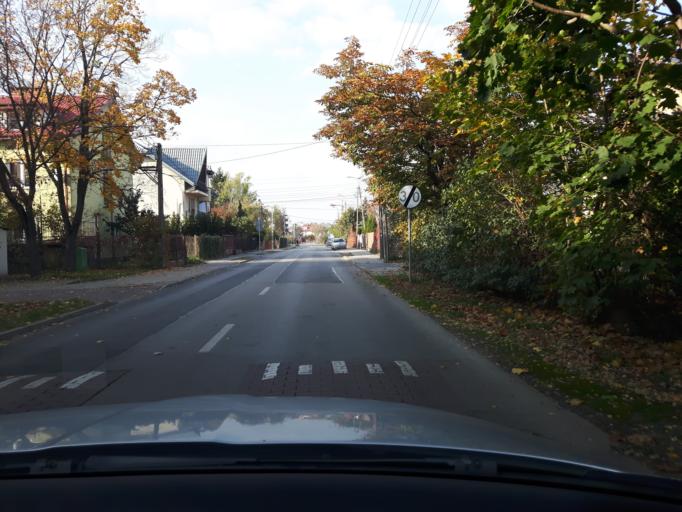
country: PL
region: Masovian Voivodeship
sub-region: Warszawa
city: Bialoleka
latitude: 52.3050
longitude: 20.9801
